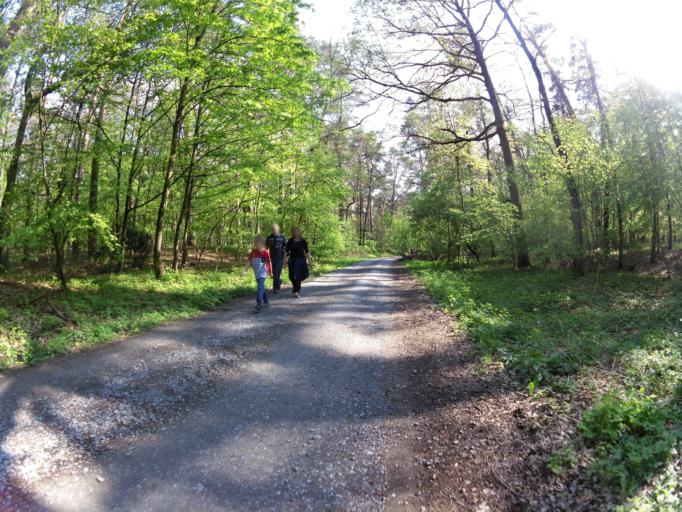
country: DE
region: Bavaria
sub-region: Regierungsbezirk Unterfranken
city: Sommerhausen
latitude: 49.7054
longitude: 10.0526
